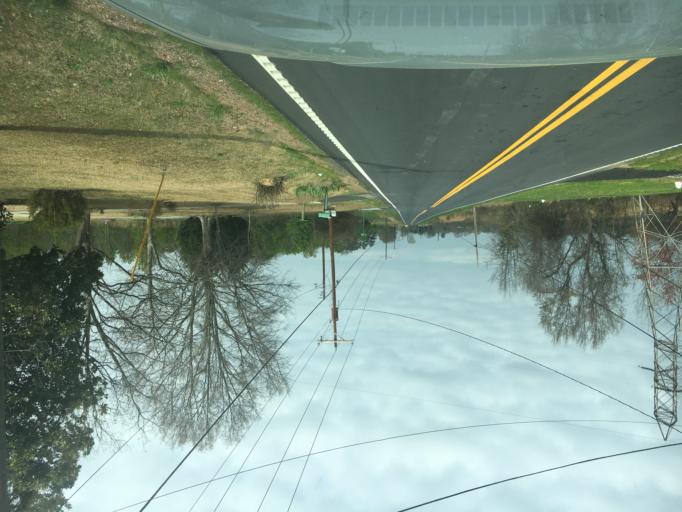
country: US
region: South Carolina
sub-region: Spartanburg County
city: Inman Mills
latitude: 35.0380
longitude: -82.1306
